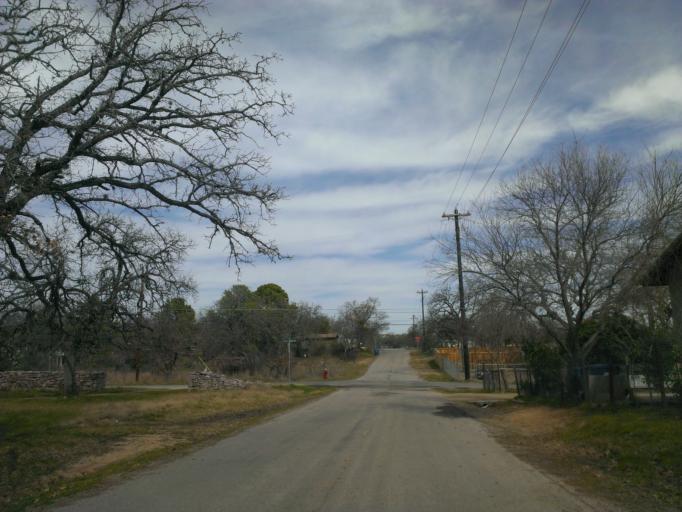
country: US
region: Texas
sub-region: Burnet County
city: Granite Shoals
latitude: 30.5930
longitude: -98.3801
